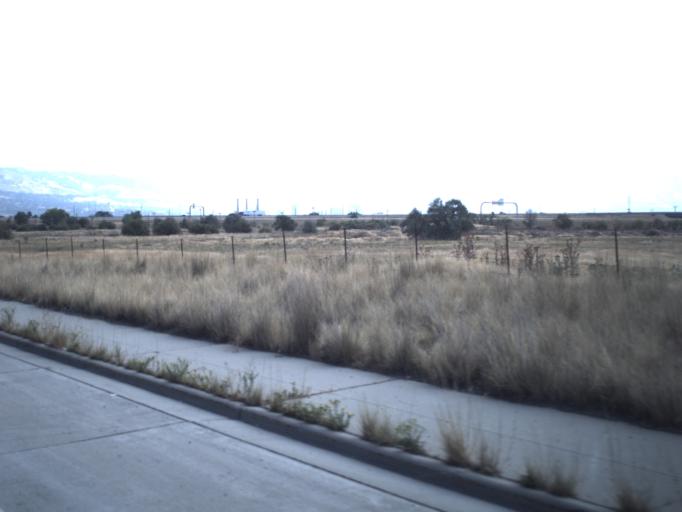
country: US
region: Utah
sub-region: Salt Lake County
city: Salt Lake City
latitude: 40.7682
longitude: -111.9577
